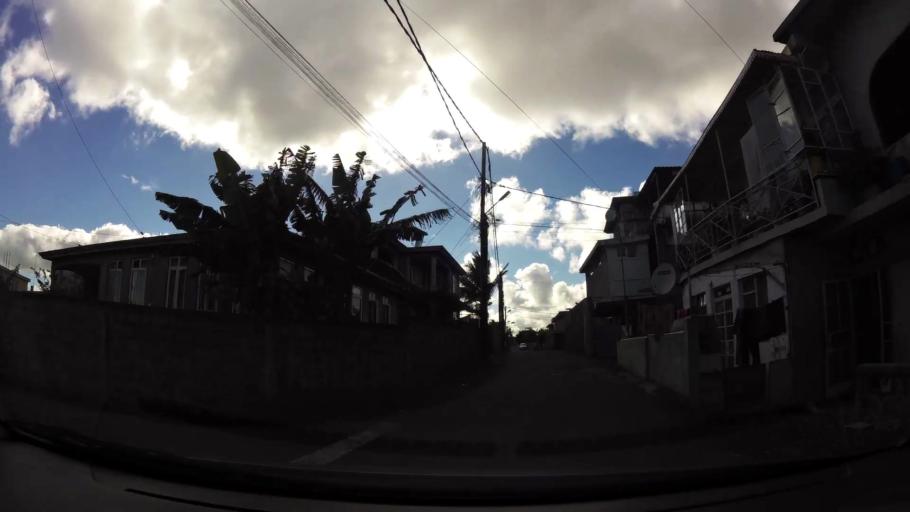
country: MU
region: Plaines Wilhems
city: Curepipe
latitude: -20.2994
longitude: 57.5142
